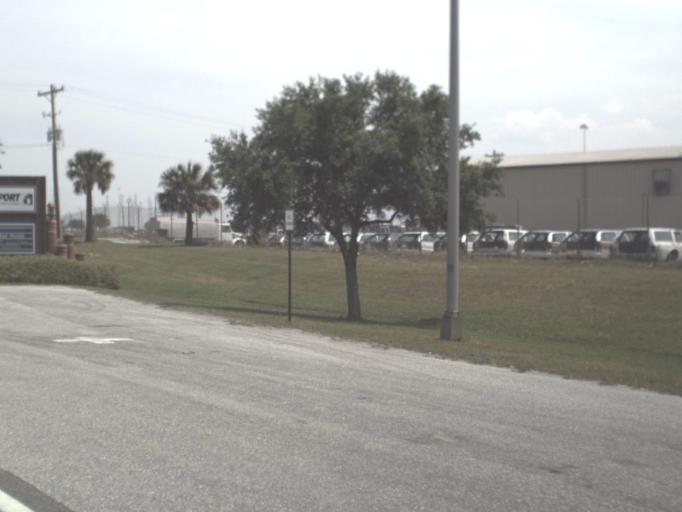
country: US
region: Florida
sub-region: Duval County
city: Jacksonville
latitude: 30.4101
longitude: -81.5390
